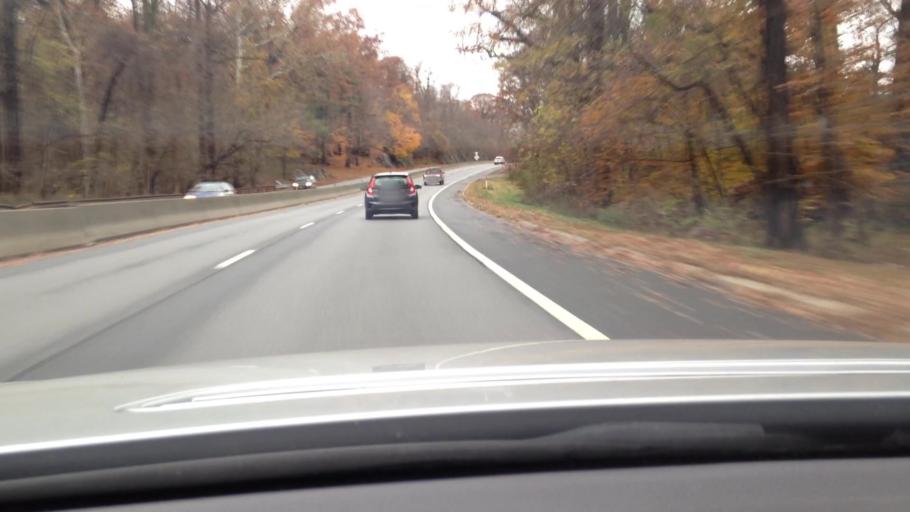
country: US
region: New York
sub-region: Westchester County
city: Elmsford
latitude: 41.0654
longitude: -73.8253
